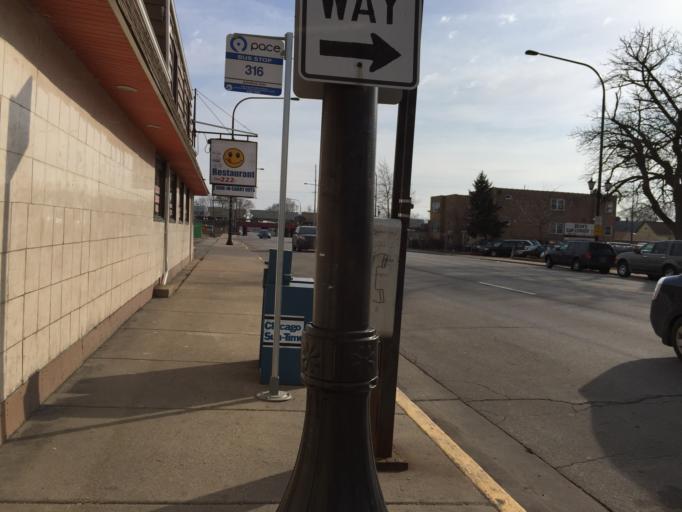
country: US
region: Illinois
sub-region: Cook County
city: Cicero
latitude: 41.8346
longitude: -87.7535
